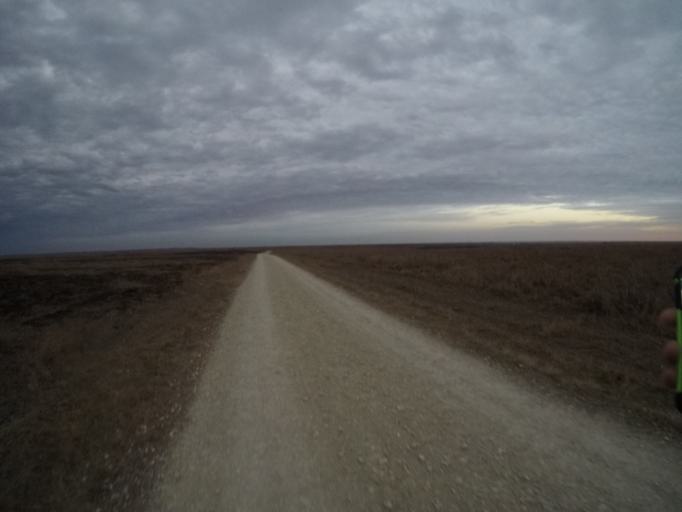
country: US
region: Kansas
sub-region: Chase County
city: Cottonwood Falls
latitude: 38.4369
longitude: -96.5778
